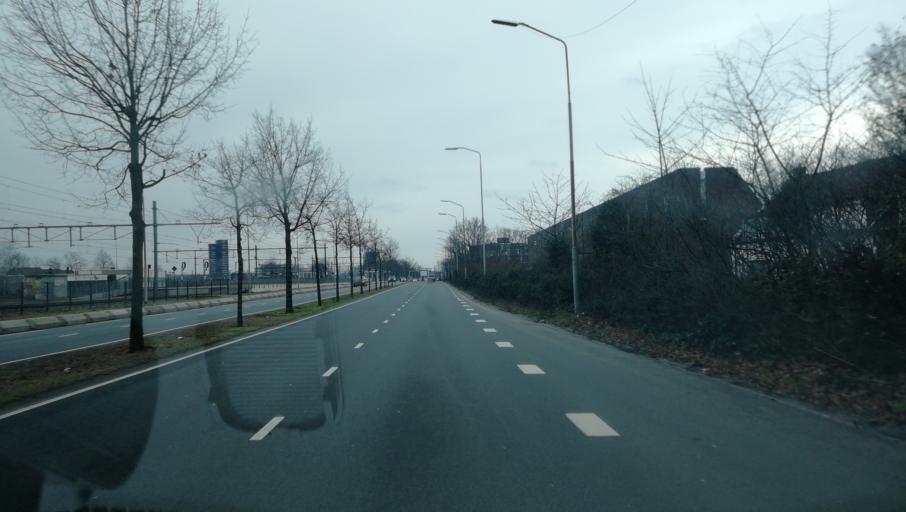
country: NL
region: Limburg
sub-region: Gemeente Venlo
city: Venlo
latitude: 51.3738
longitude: 6.1525
